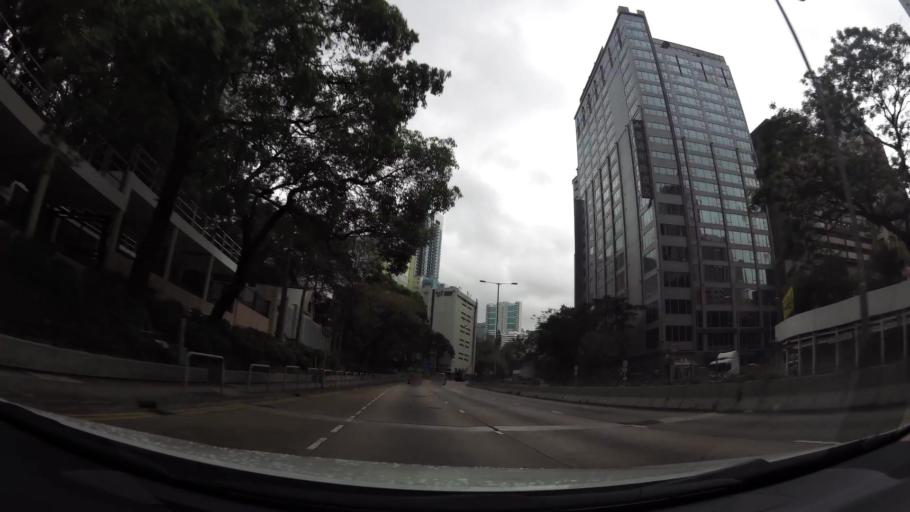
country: HK
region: Tsuen Wan
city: Tsuen Wan
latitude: 22.3710
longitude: 114.1289
